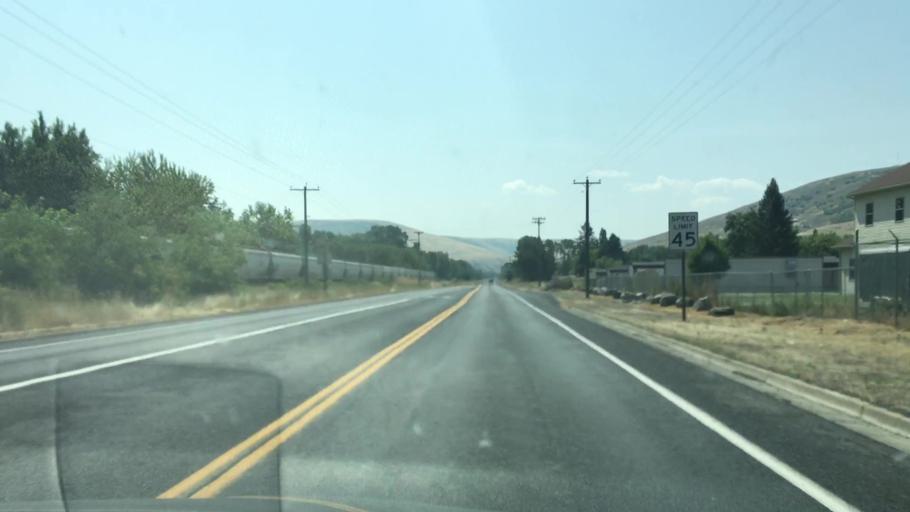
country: US
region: Idaho
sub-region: Nez Perce County
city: Lapwai
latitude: 46.4001
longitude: -116.8008
